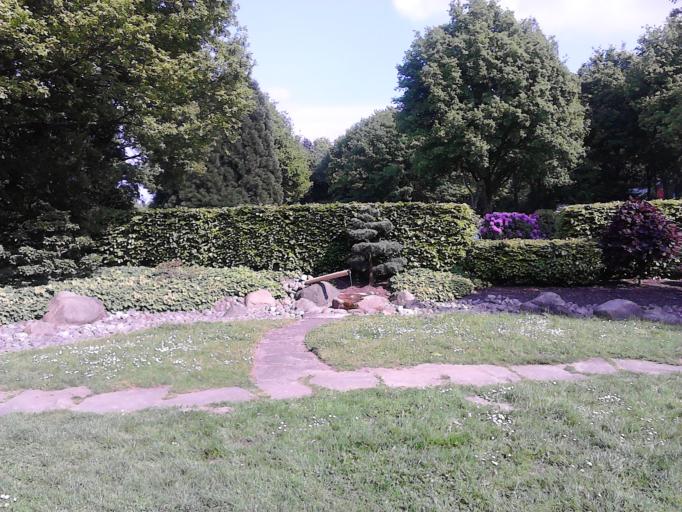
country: DE
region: Lower Saxony
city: Lilienthal
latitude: 53.0945
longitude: 8.8827
